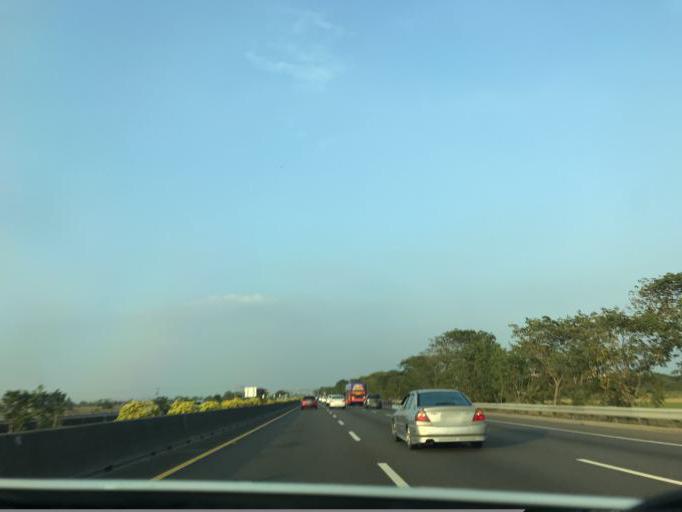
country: TW
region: Taiwan
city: Xinying
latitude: 23.3155
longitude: 120.2960
